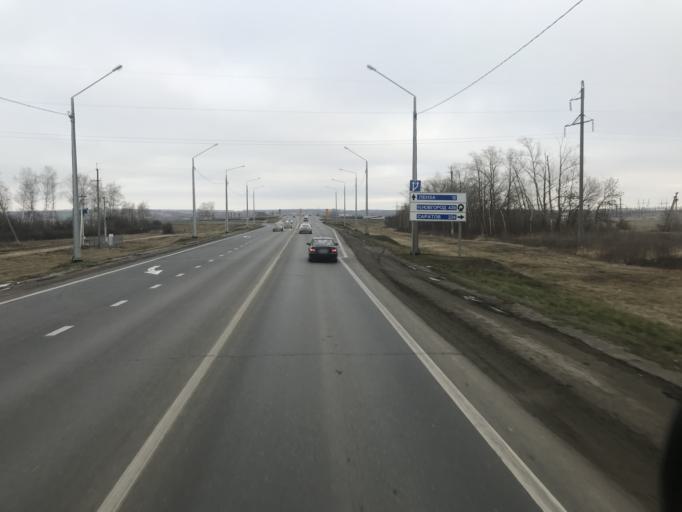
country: RU
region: Penza
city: Bogoslovka
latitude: 53.1308
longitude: 44.7718
